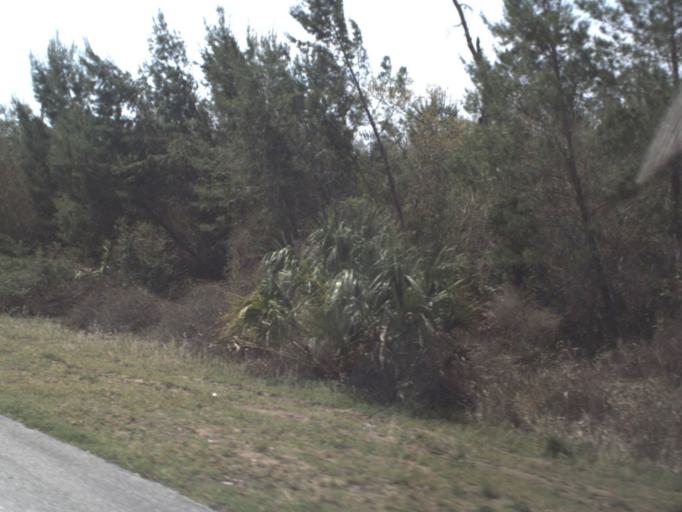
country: US
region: Florida
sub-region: Lake County
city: Astor
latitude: 29.2017
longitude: -81.6585
